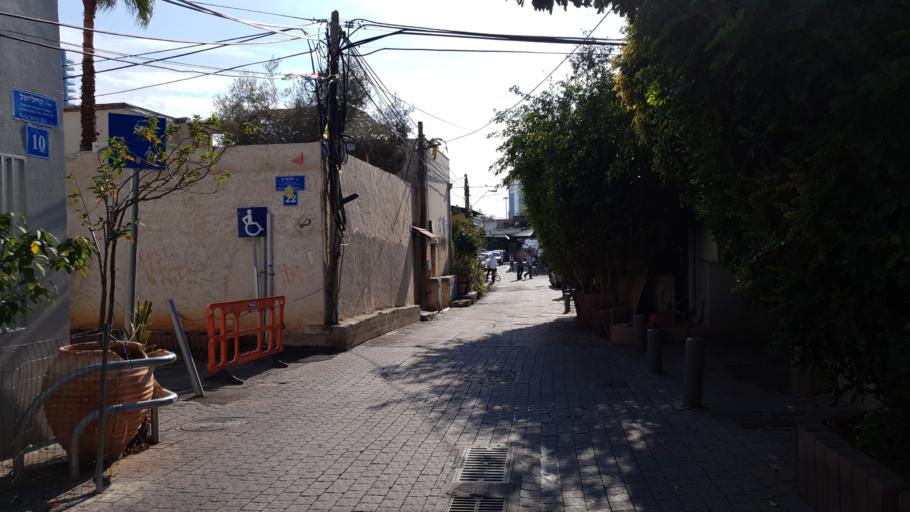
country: IL
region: Tel Aviv
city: Tel Aviv
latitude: 32.0685
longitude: 34.7671
